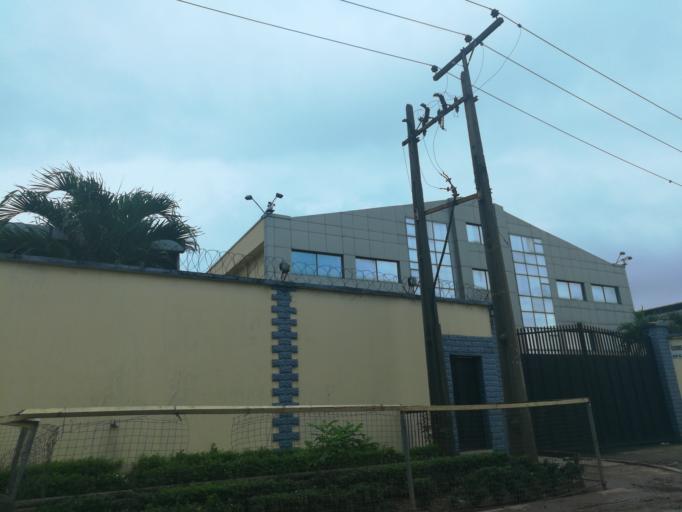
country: NG
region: Lagos
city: Ikeja
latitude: 6.6123
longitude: 3.3418
